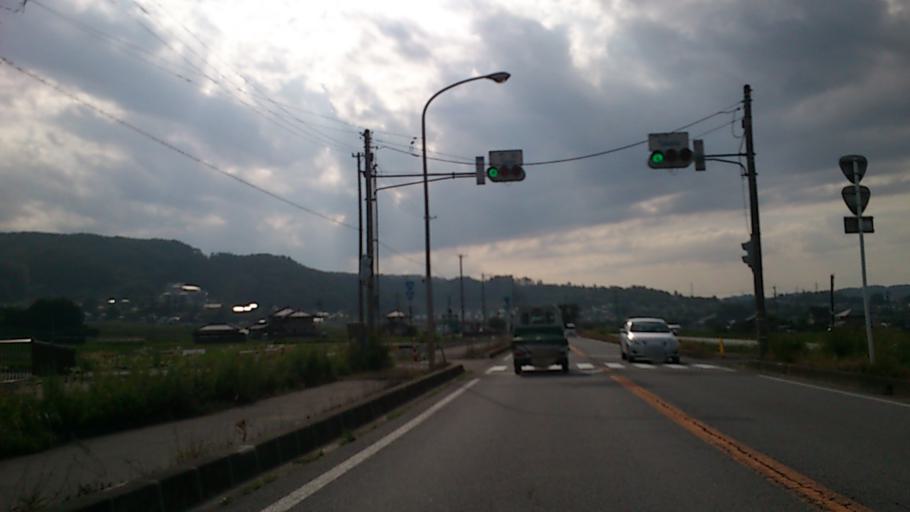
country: JP
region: Nagano
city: Saku
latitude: 36.2406
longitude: 138.4302
